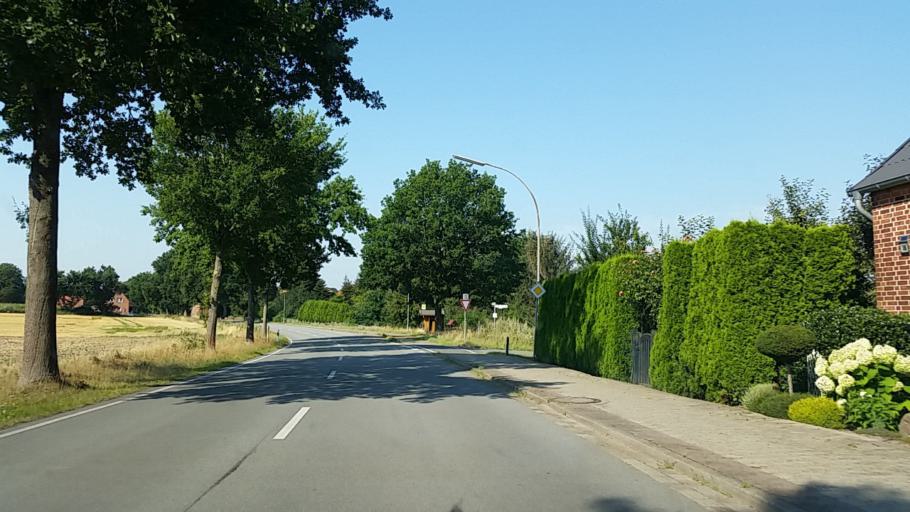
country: DE
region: Lower Saxony
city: Luder
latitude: 52.8285
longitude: 10.6383
